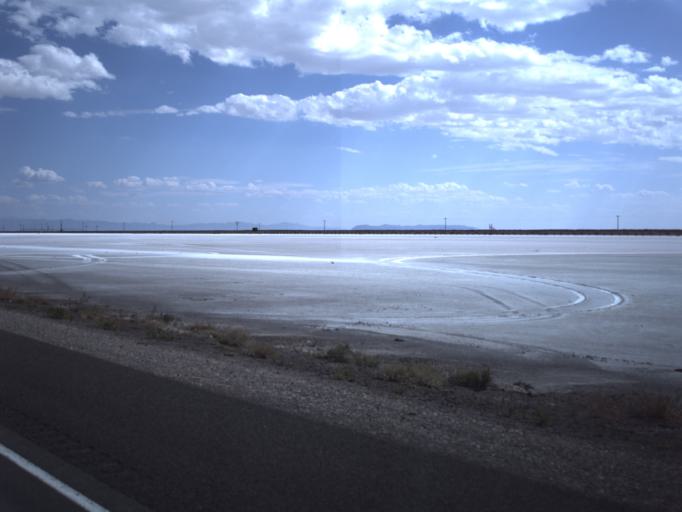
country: US
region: Utah
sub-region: Tooele County
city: Wendover
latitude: 40.7348
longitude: -113.6733
